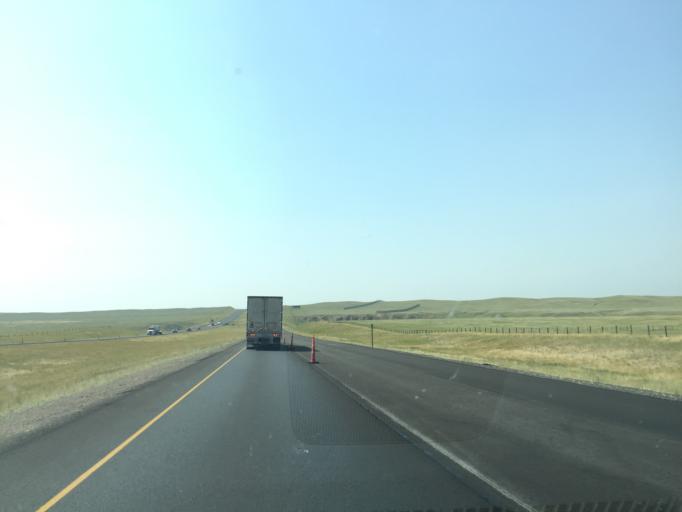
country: US
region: Wyoming
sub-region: Laramie County
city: Ranchettes
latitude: 41.3297
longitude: -104.8636
